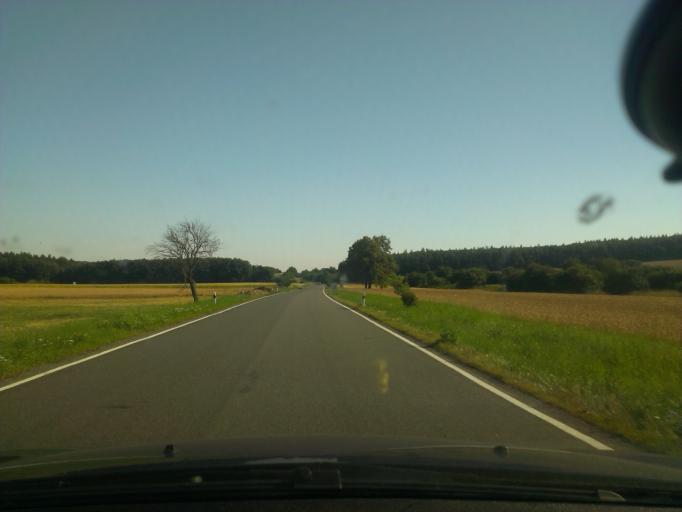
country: CZ
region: South Moravian
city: Velka nad Velickou
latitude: 48.8381
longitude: 17.5191
